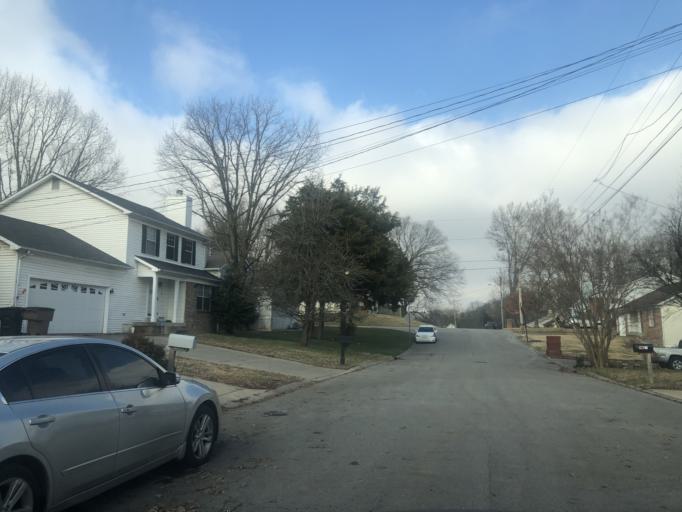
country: US
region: Tennessee
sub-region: Rutherford County
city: La Vergne
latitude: 36.0823
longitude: -86.6578
